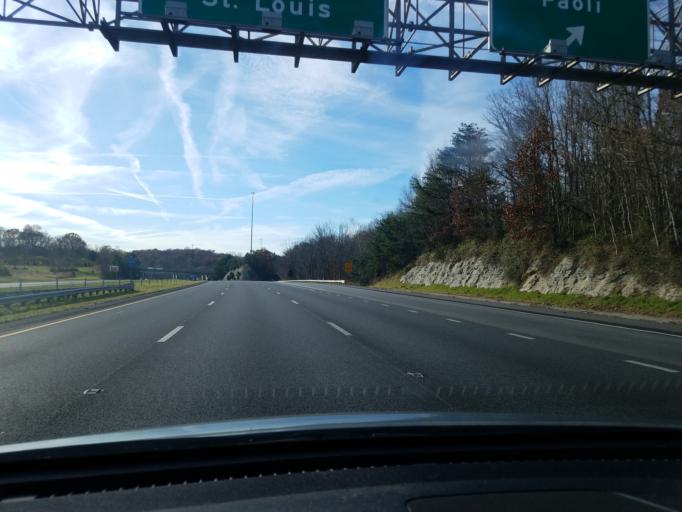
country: US
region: Indiana
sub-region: Floyd County
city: New Albany
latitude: 38.3041
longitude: -85.8859
